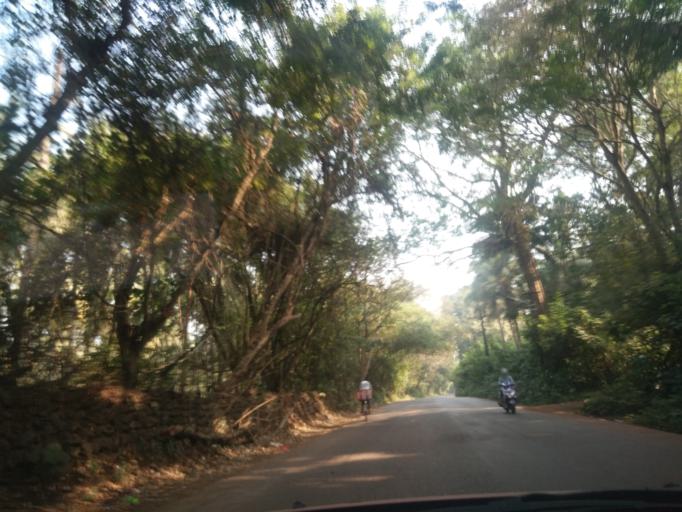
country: IN
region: Goa
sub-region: North Goa
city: Curti
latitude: 15.4223
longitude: 74.0525
